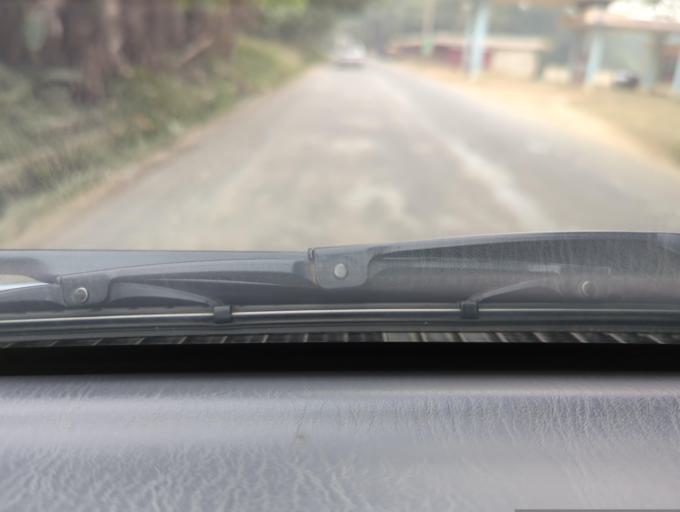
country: BD
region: Sylhet
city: Maulavi Bazar
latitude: 24.5162
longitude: 91.7279
